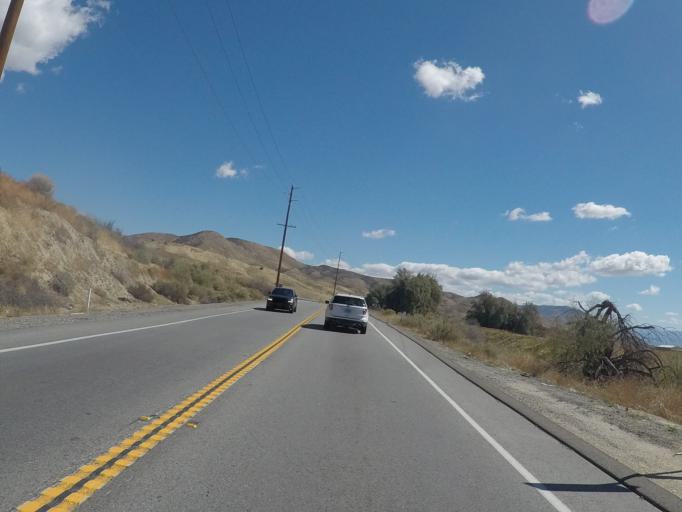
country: US
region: California
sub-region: Riverside County
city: Lakeview
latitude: 33.8900
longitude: -117.0734
